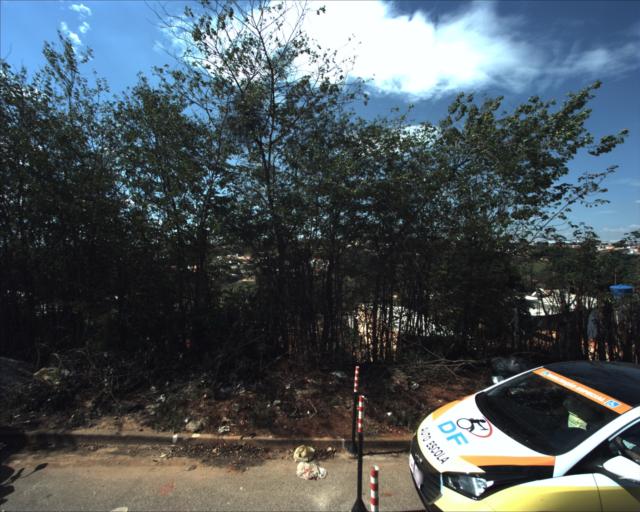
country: BR
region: Sao Paulo
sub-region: Sorocaba
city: Sorocaba
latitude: -23.4783
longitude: -47.5081
